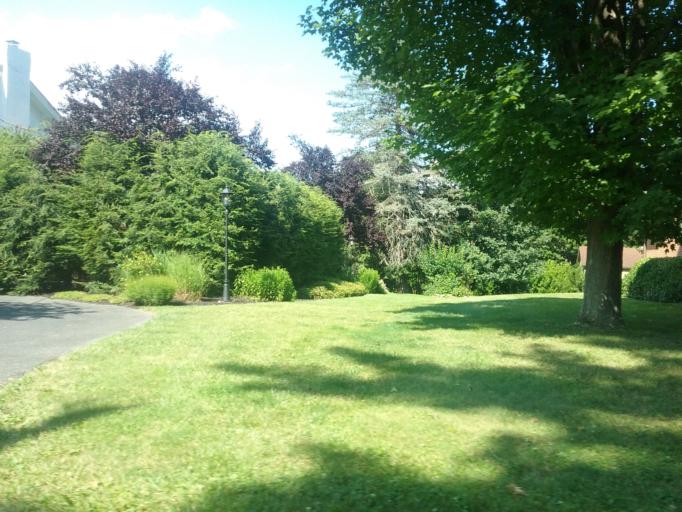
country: US
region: Pennsylvania
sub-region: Tioga County
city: Wellsboro
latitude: 41.7438
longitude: -77.3025
